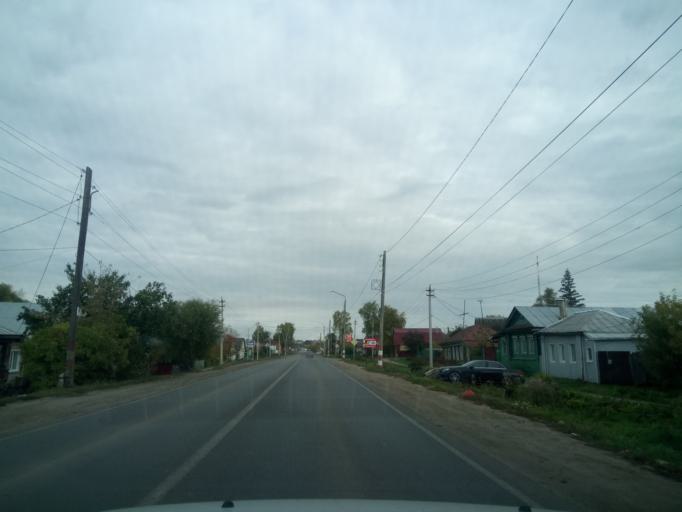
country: RU
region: Nizjnij Novgorod
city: Lukoyanov
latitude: 55.0312
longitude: 44.4834
